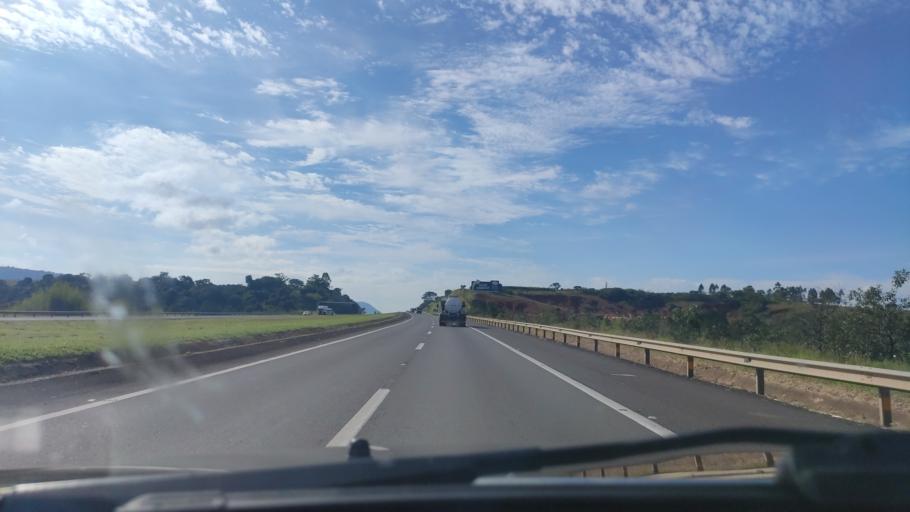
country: BR
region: Sao Paulo
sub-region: Itatinga
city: Itatinga
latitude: -23.1347
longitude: -48.4586
